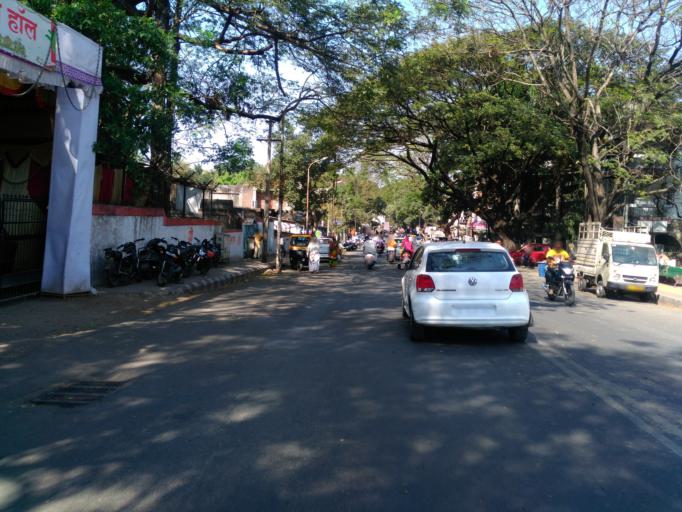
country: IN
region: Maharashtra
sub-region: Pune Division
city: Pune
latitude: 18.4877
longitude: 73.8499
